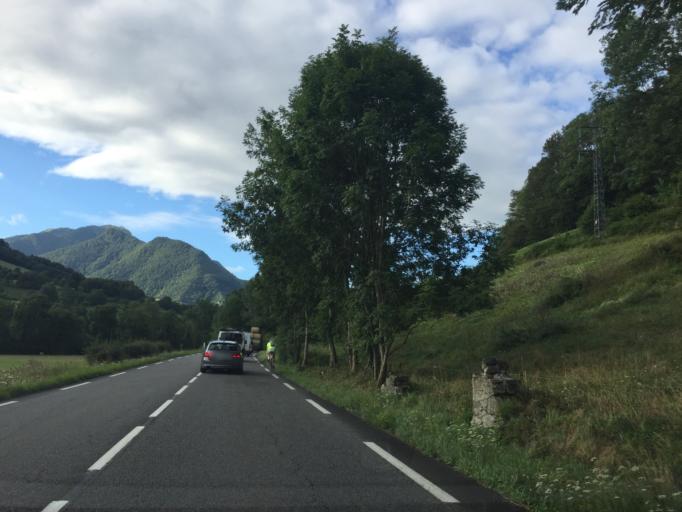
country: FR
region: Midi-Pyrenees
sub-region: Departement des Hautes-Pyrenees
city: La Barthe-de-Neste
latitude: 42.9871
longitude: 0.3755
